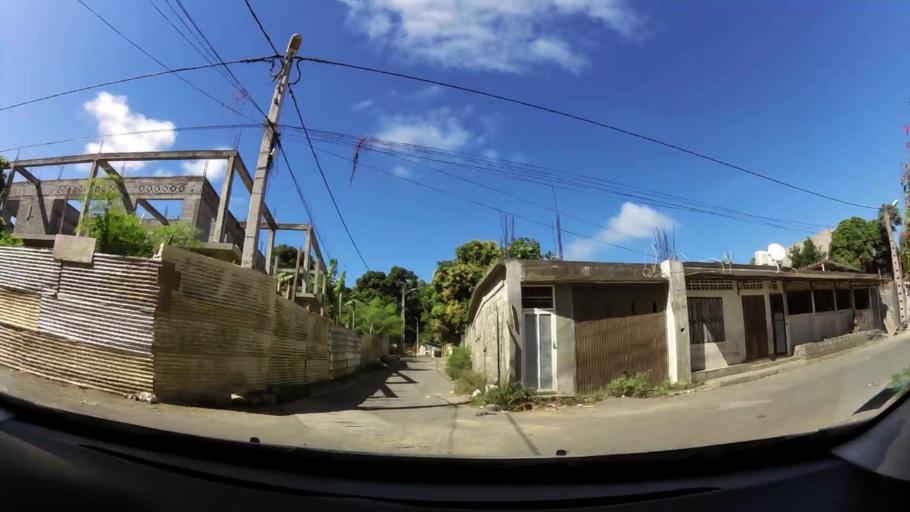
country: YT
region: Pamandzi
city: Pamandzi
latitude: -12.7900
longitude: 45.2809
